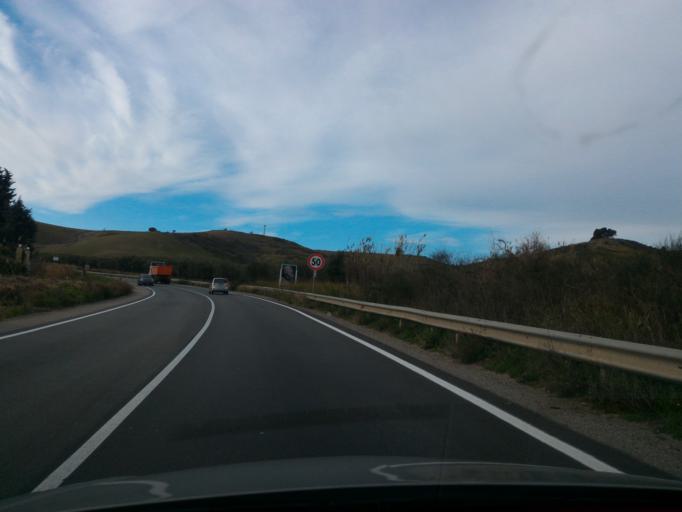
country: IT
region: Calabria
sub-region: Provincia di Crotone
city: Crotone
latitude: 39.0527
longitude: 17.0743
